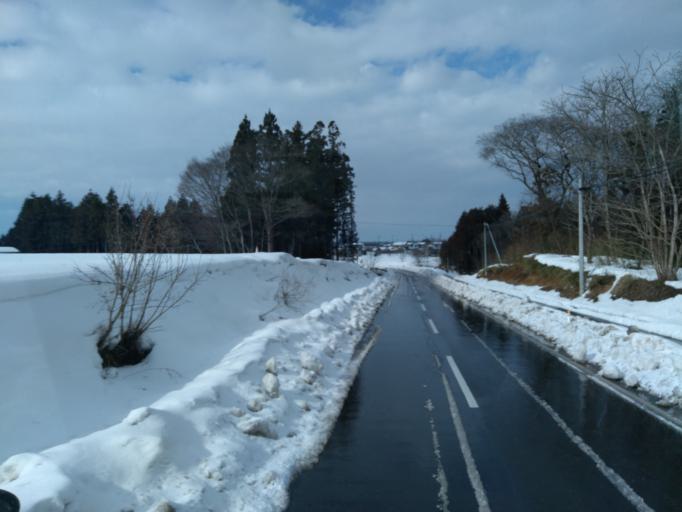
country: JP
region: Iwate
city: Mizusawa
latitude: 39.1309
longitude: 141.1901
